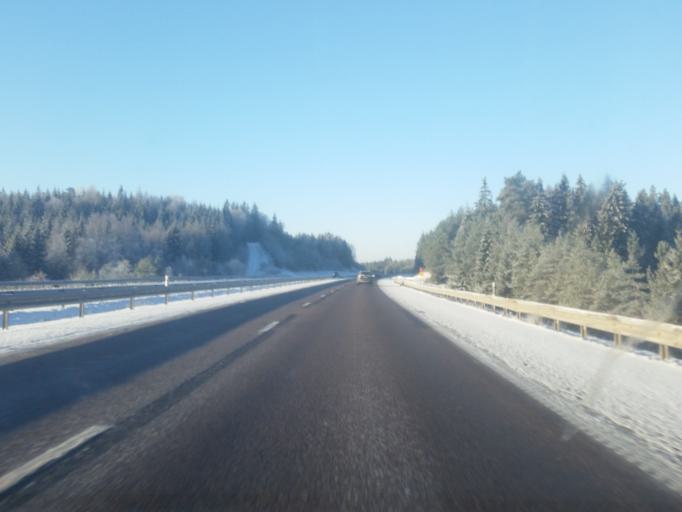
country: SE
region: Vaestra Goetaland
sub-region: Bollebygds Kommun
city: Bollebygd
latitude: 57.6703
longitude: 12.6429
